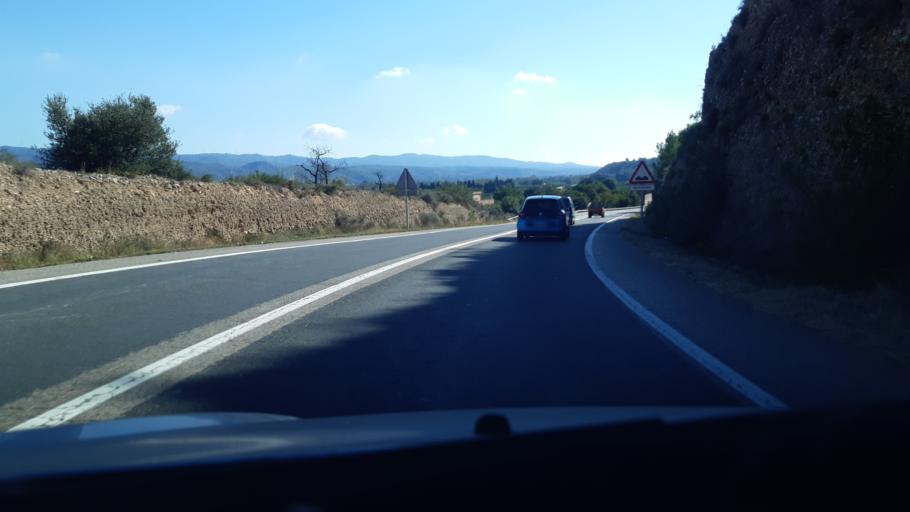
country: ES
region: Catalonia
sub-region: Provincia de Tarragona
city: Tivenys
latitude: 40.8780
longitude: 0.4997
